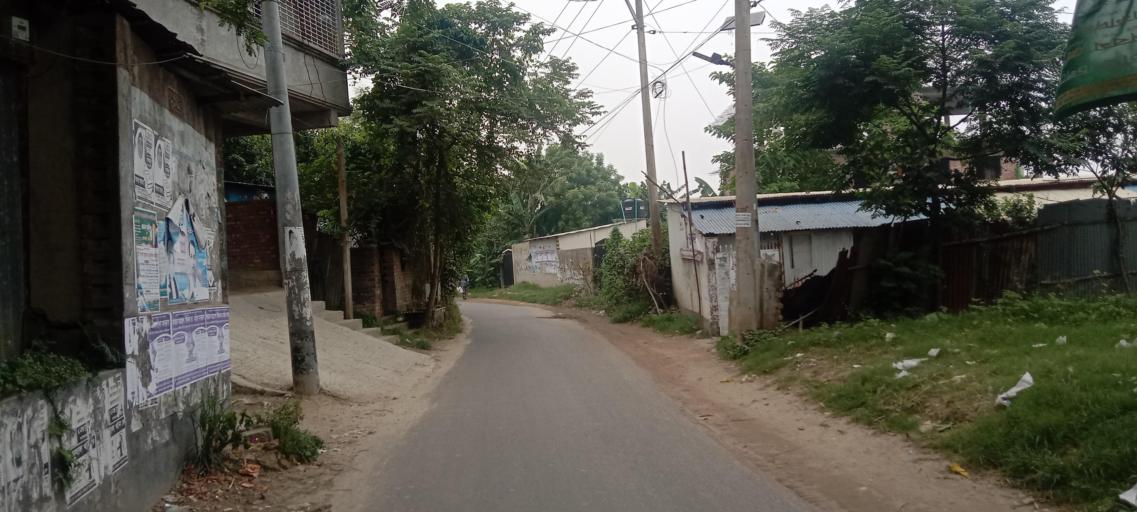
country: BD
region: Dhaka
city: Azimpur
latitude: 23.7346
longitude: 90.3226
